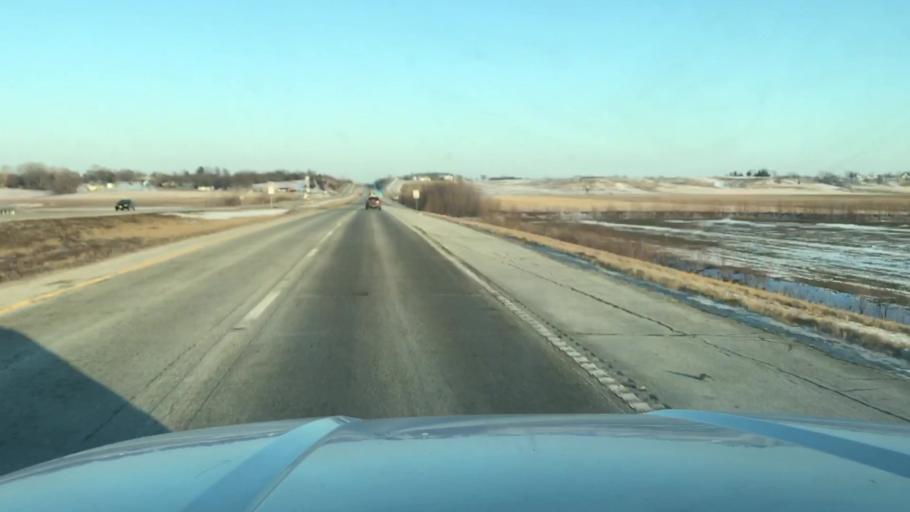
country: US
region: Missouri
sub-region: Buchanan County
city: Saint Joseph
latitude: 39.7478
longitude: -94.7239
